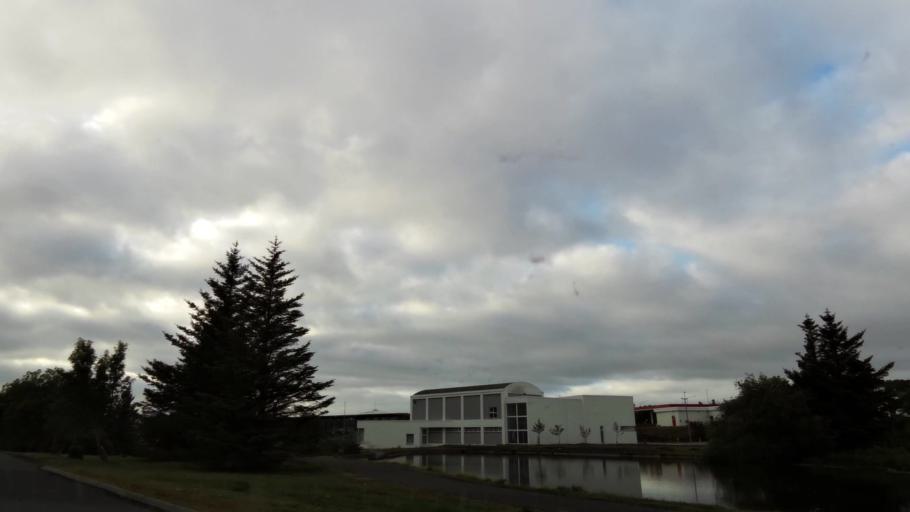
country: IS
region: Capital Region
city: Hafnarfjoerdur
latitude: 64.0655
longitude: -21.9400
